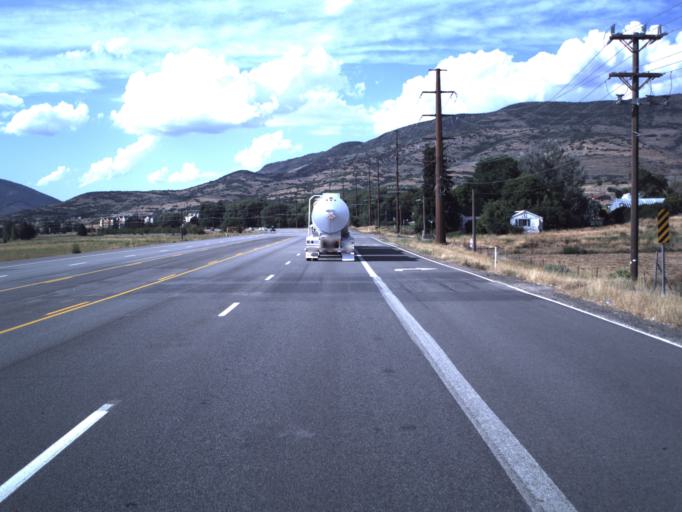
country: US
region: Utah
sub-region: Wasatch County
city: Heber
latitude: 40.5297
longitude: -111.4094
